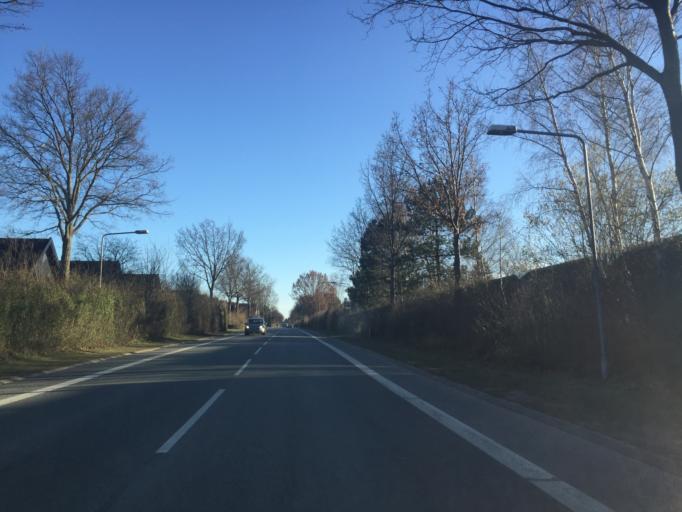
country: DK
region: Capital Region
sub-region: Dragor Kommune
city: Dragor
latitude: 55.5979
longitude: 12.6583
